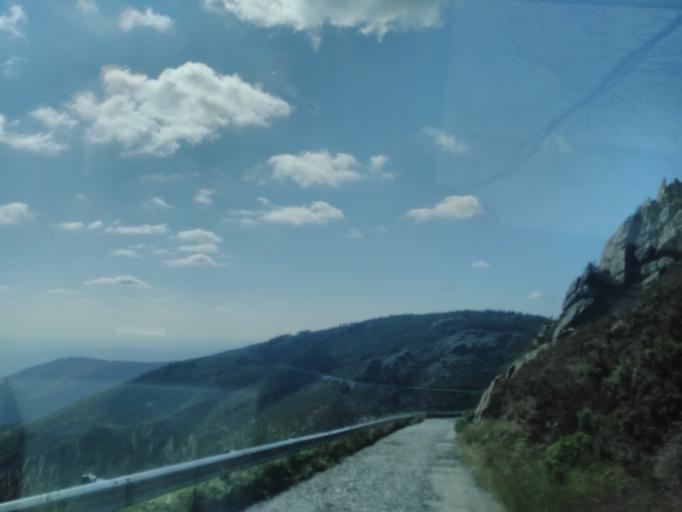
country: PT
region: Vila Real
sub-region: Mesao Frio
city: Mesao Frio
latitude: 41.2672
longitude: -7.9064
